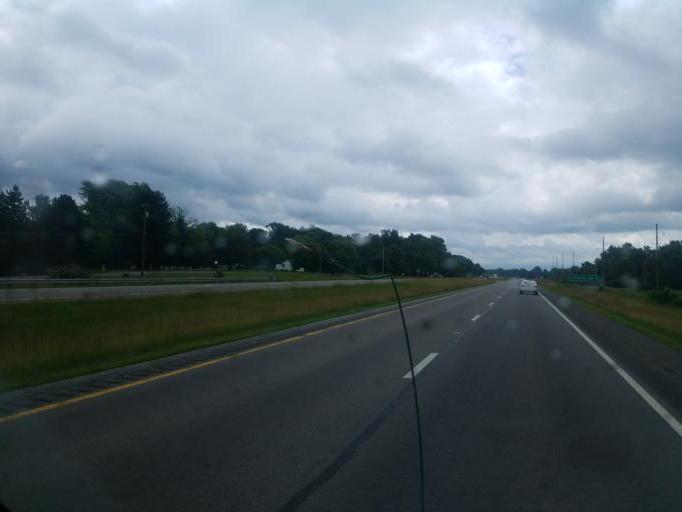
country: US
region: Ohio
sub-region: Logan County
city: Bellefontaine
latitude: 40.4136
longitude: -83.7926
